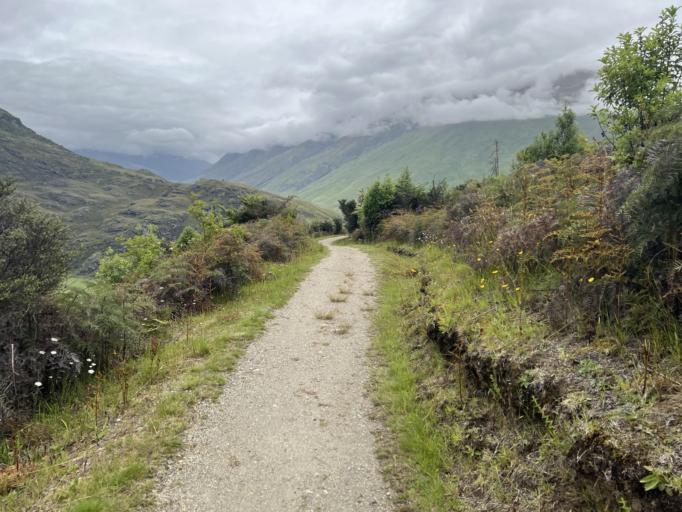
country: NZ
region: Otago
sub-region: Queenstown-Lakes District
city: Wanaka
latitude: -44.6454
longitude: 168.9678
